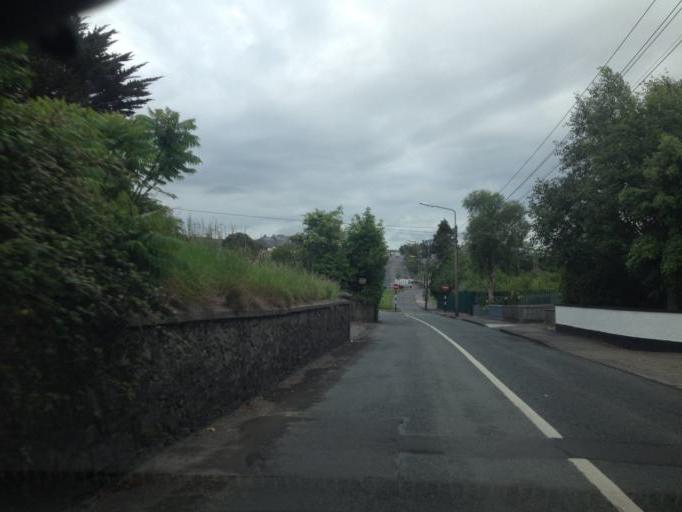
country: IE
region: Connaught
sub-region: Sligo
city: Sligo
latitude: 54.2798
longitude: -8.4751
